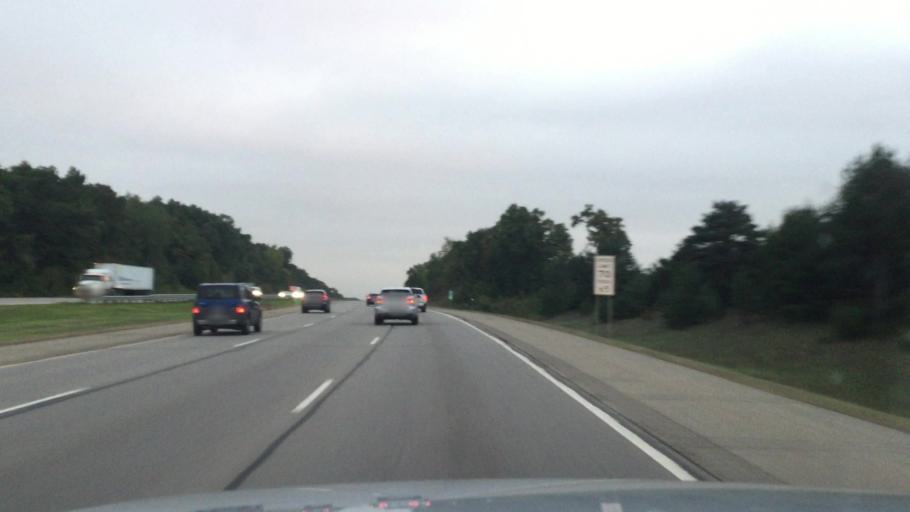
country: US
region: Michigan
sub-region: Oakland County
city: Holly
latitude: 42.8230
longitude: -83.5708
